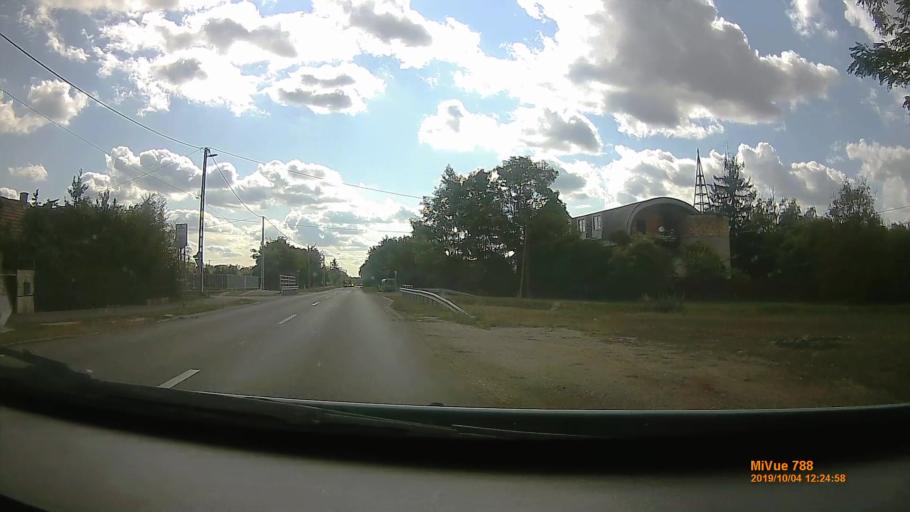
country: HU
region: Szabolcs-Szatmar-Bereg
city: Nyiregyhaza
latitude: 47.9910
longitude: 21.7039
